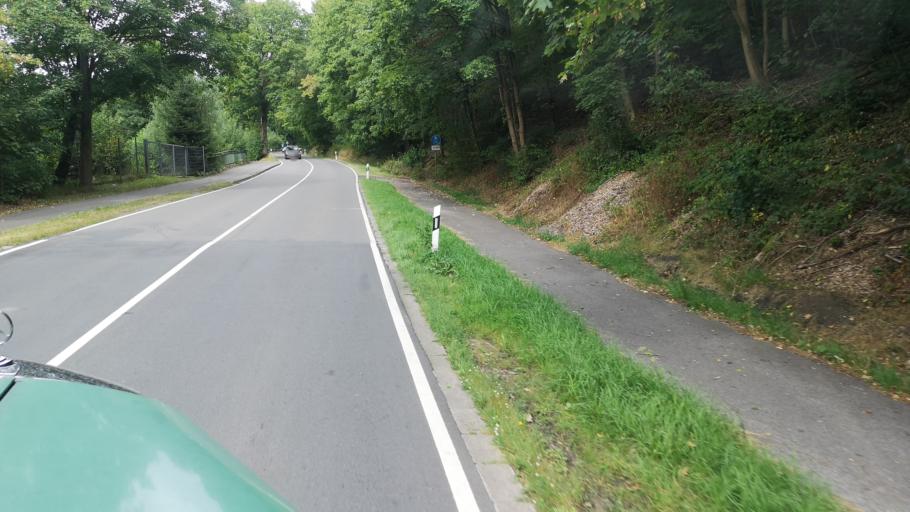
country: DE
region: North Rhine-Westphalia
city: Radevormwald
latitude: 51.1892
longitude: 7.3178
